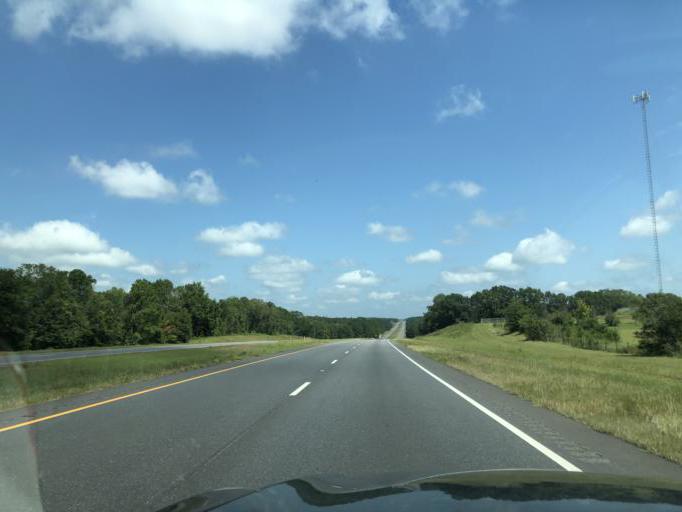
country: US
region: Alabama
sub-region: Henry County
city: Headland
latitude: 31.4571
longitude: -85.3089
